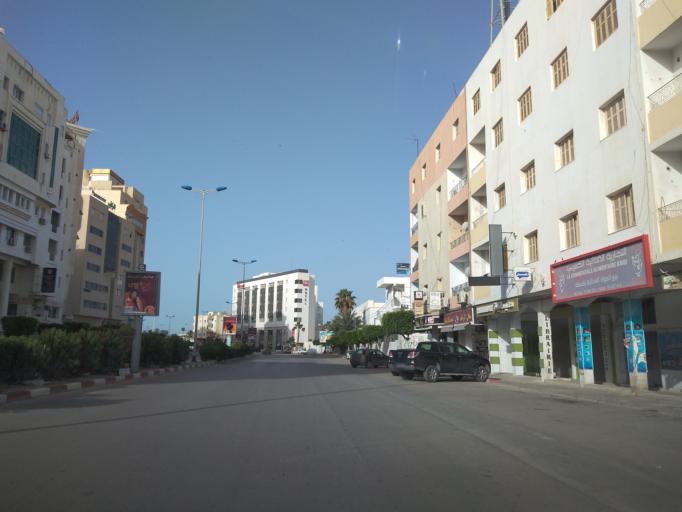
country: TN
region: Safaqis
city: Sfax
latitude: 34.7379
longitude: 10.7500
